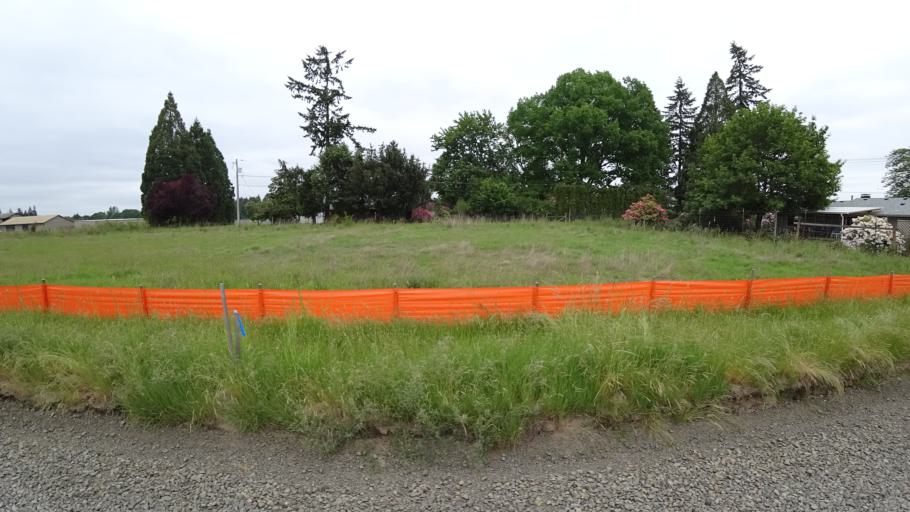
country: US
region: Oregon
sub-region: Washington County
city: Aloha
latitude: 45.4868
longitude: -122.9136
